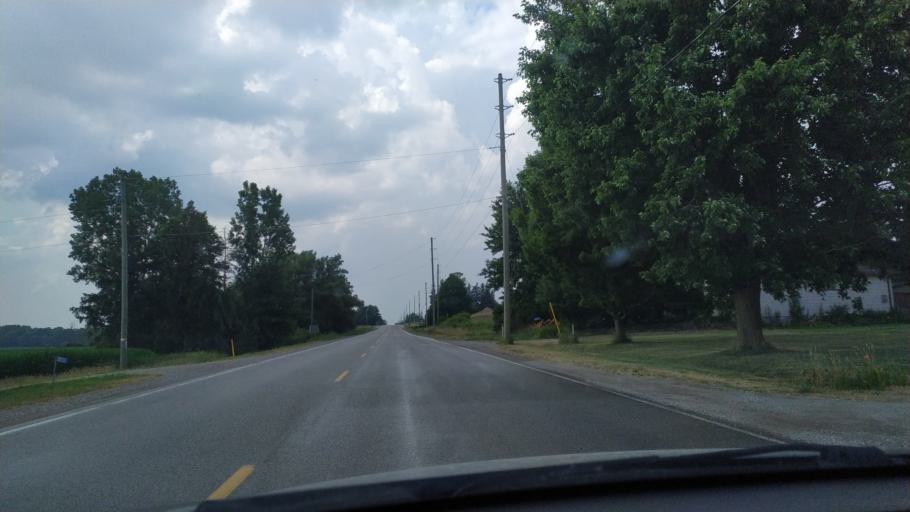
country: CA
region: Ontario
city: London
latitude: 43.1036
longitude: -81.1577
